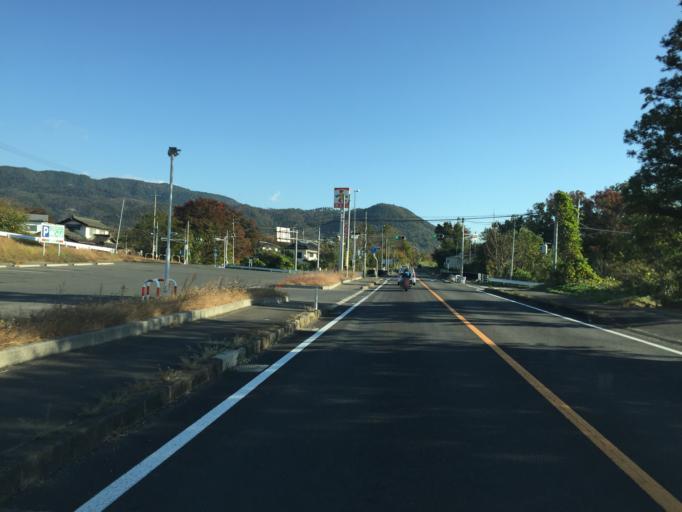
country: JP
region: Fukushima
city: Yanagawamachi-saiwaicho
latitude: 37.8806
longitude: 140.5536
